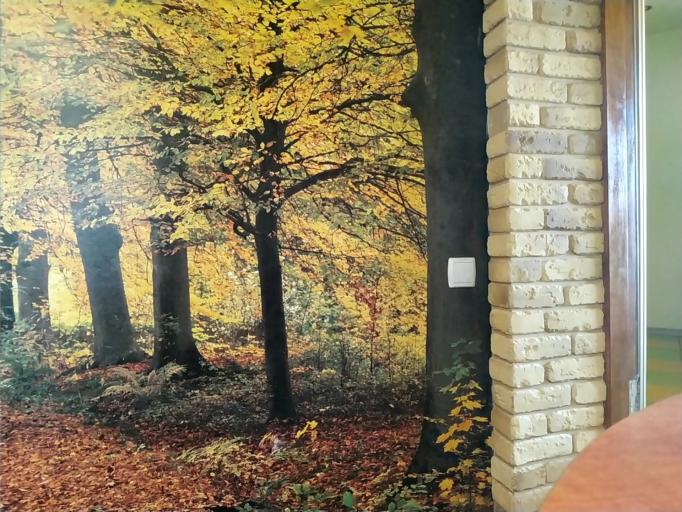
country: RU
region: Arkhangelskaya
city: Kargopol'
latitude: 60.8017
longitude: 38.8893
